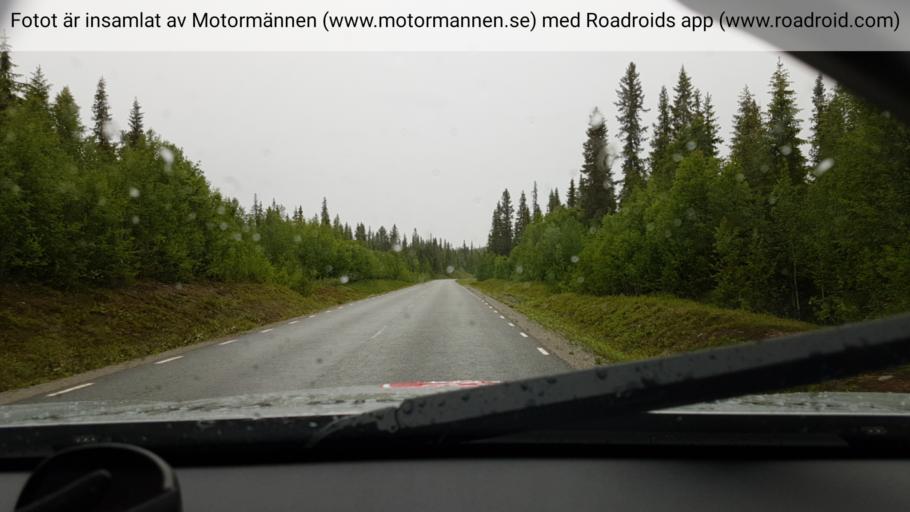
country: SE
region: Vaesterbotten
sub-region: Storumans Kommun
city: Fristad
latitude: 65.9117
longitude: 16.3099
